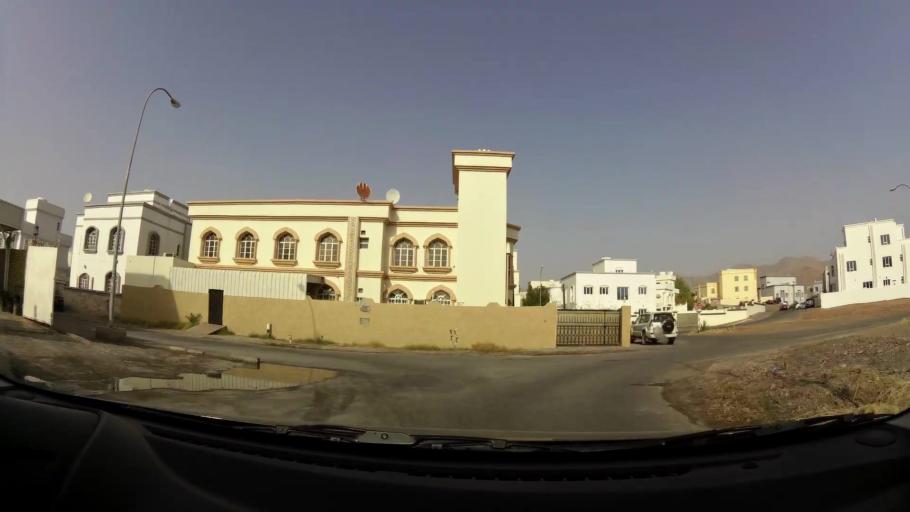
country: OM
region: Muhafazat Masqat
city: Bawshar
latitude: 23.5449
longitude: 58.3639
